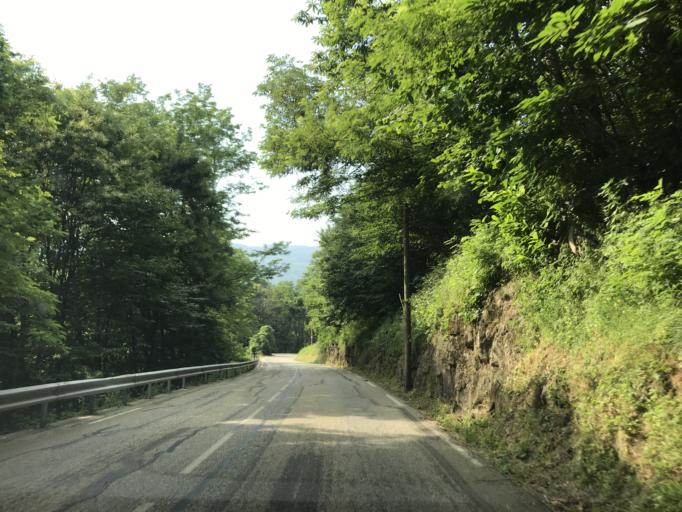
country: FR
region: Rhone-Alpes
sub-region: Departement de l'Isere
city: Allevard
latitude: 45.3868
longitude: 6.0849
